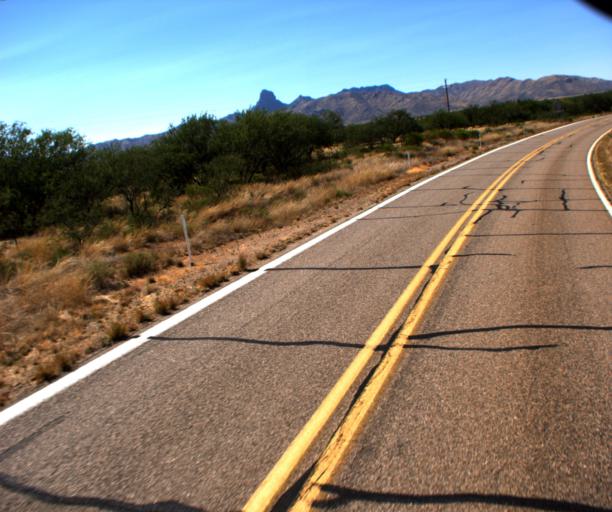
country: US
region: Arizona
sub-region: Pima County
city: Three Points
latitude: 31.6855
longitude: -111.4874
